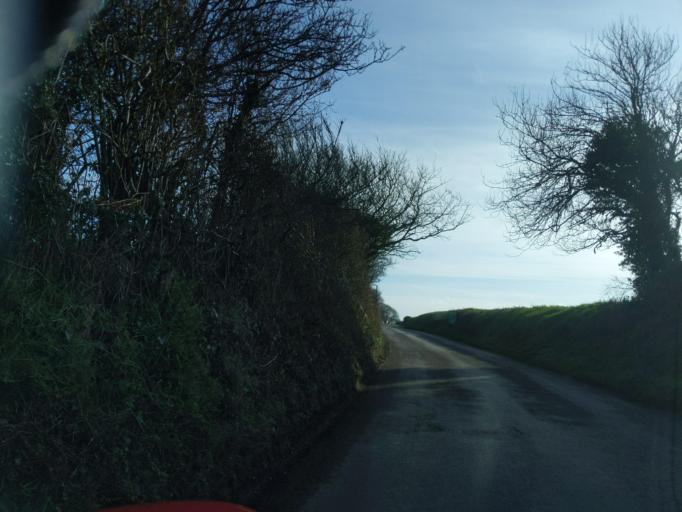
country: GB
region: England
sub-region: Devon
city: Kingsbridge
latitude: 50.3295
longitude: -3.7186
